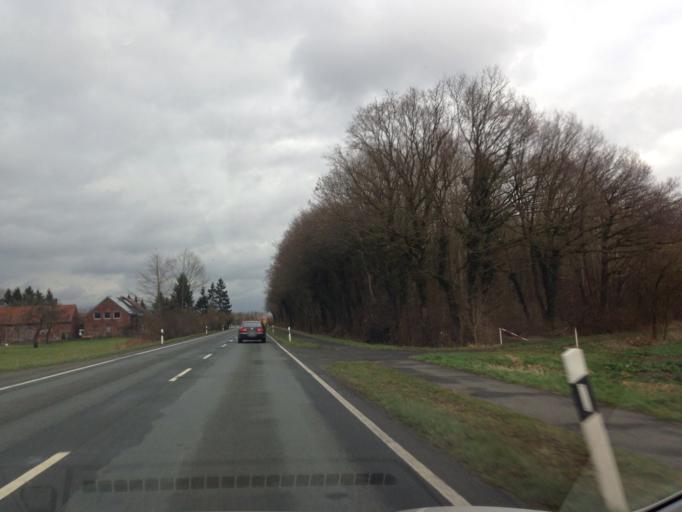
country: DE
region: North Rhine-Westphalia
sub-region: Regierungsbezirk Munster
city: Nordkirchen
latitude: 51.7444
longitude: 7.5037
